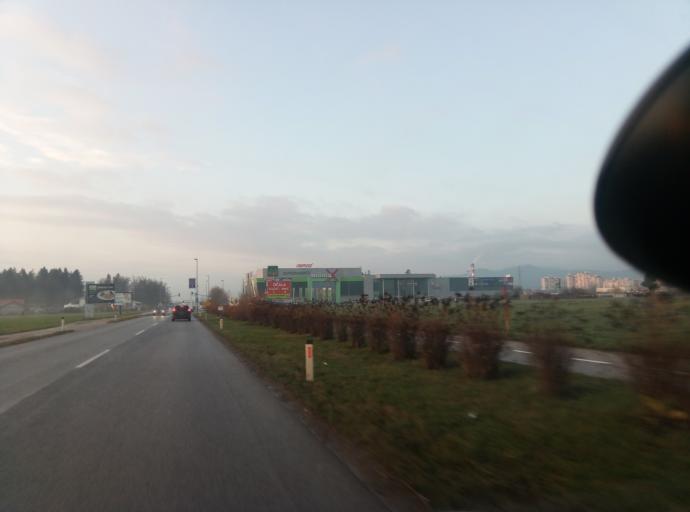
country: SI
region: Kranj
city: Kranj
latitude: 46.2386
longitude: 14.3771
